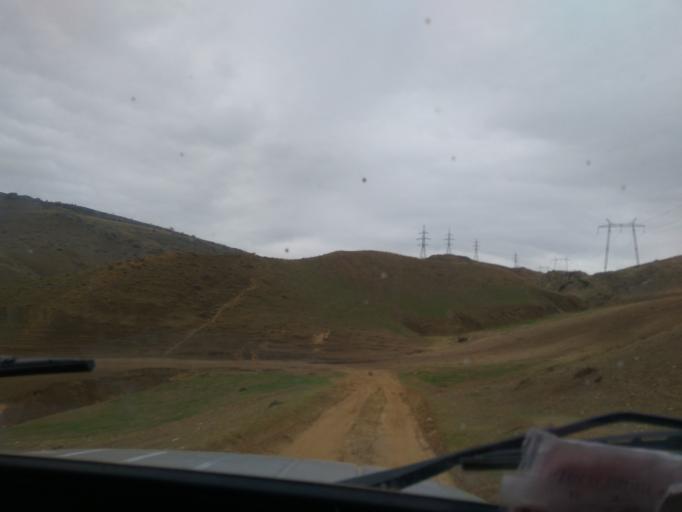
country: RU
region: Dagestan
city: Korkmaskala
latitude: 43.0035
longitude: 47.2133
